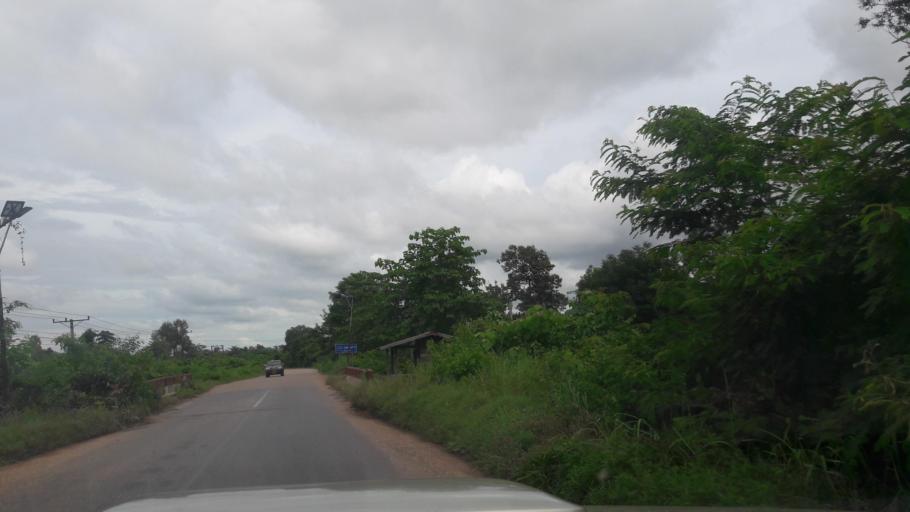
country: TH
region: Nong Khai
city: Rattanawapi
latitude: 18.2358
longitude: 103.1225
